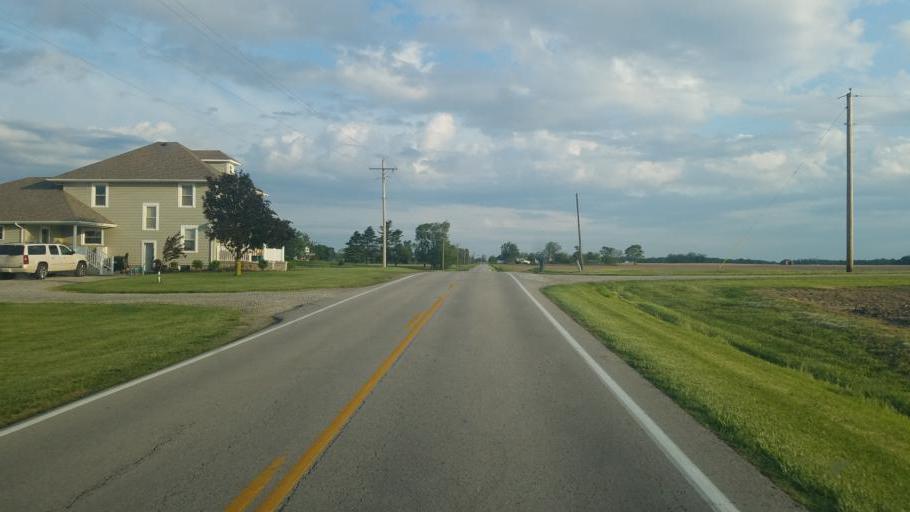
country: US
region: Ohio
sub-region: Highland County
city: Leesburg
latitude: 39.4049
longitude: -83.6041
